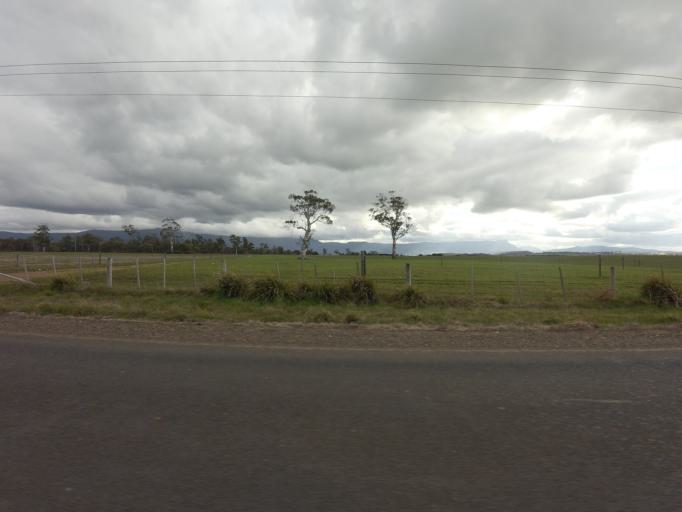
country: AU
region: Tasmania
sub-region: Northern Midlands
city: Longford
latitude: -41.7628
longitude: 147.0834
